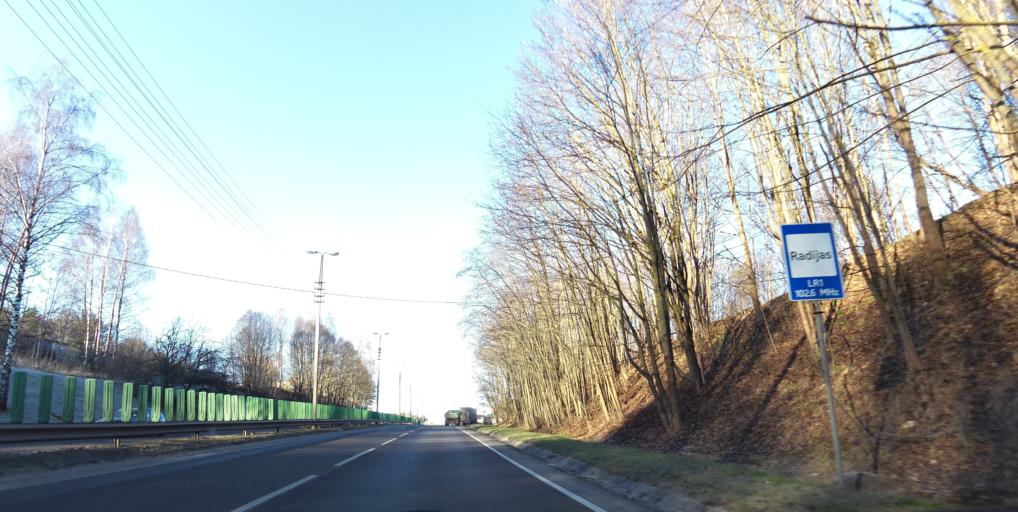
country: LT
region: Vilnius County
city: Lazdynai
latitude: 54.6394
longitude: 25.1870
